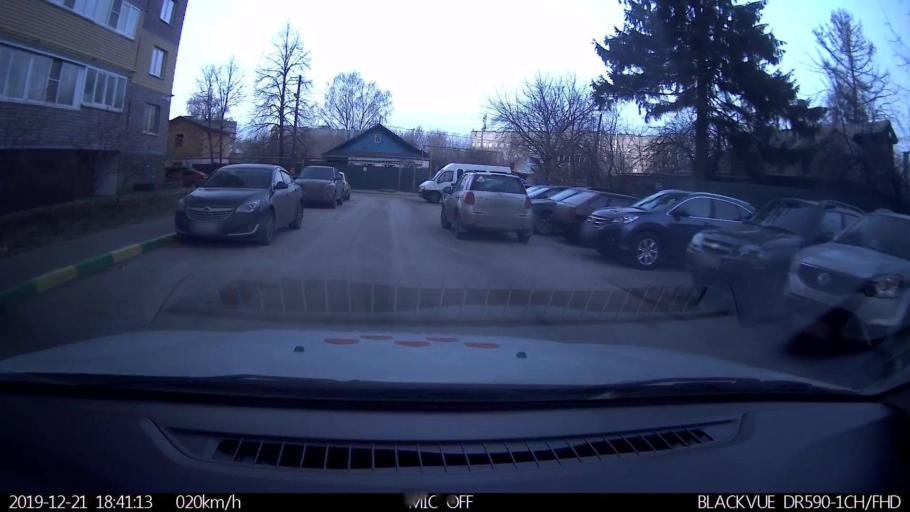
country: RU
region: Nizjnij Novgorod
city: Nizhniy Novgorod
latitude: 56.3277
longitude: 43.9263
